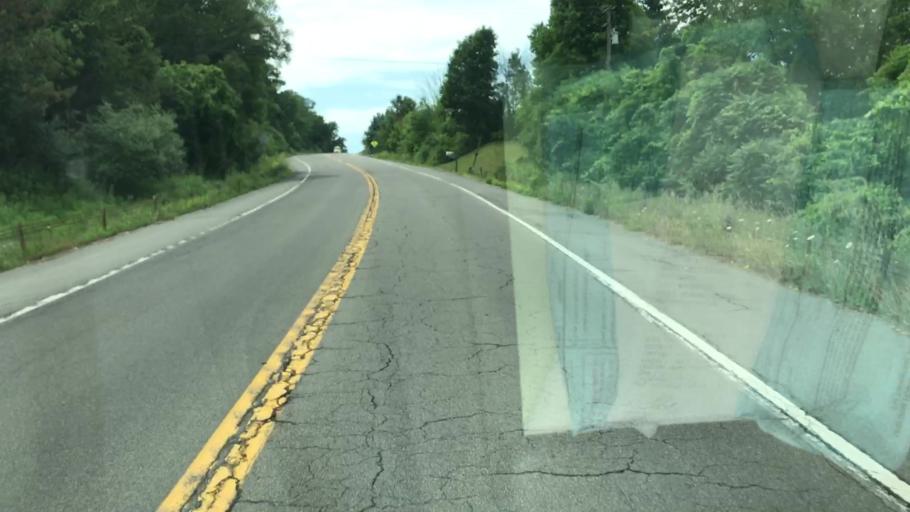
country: US
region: New York
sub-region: Onondaga County
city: Marcellus
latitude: 42.9332
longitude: -76.3444
